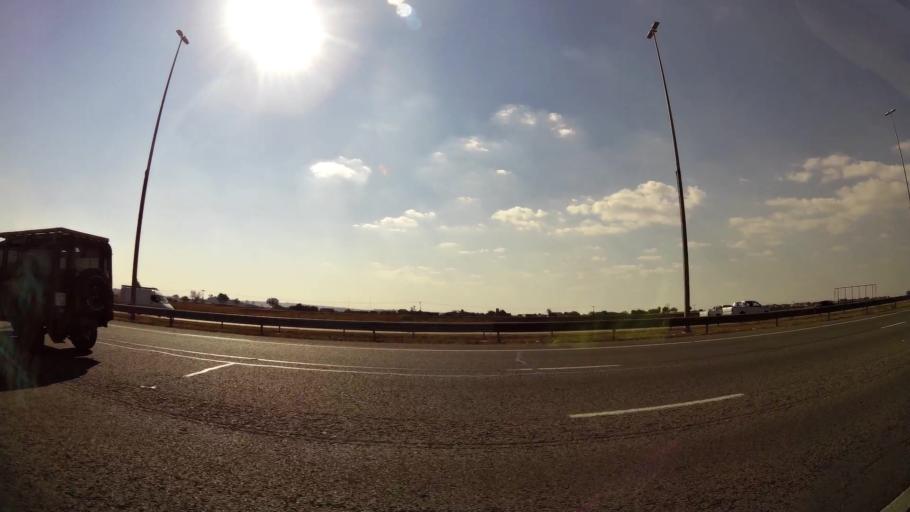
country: ZA
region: Gauteng
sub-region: Ekurhuleni Metropolitan Municipality
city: Tembisa
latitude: -26.0475
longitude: 28.2781
